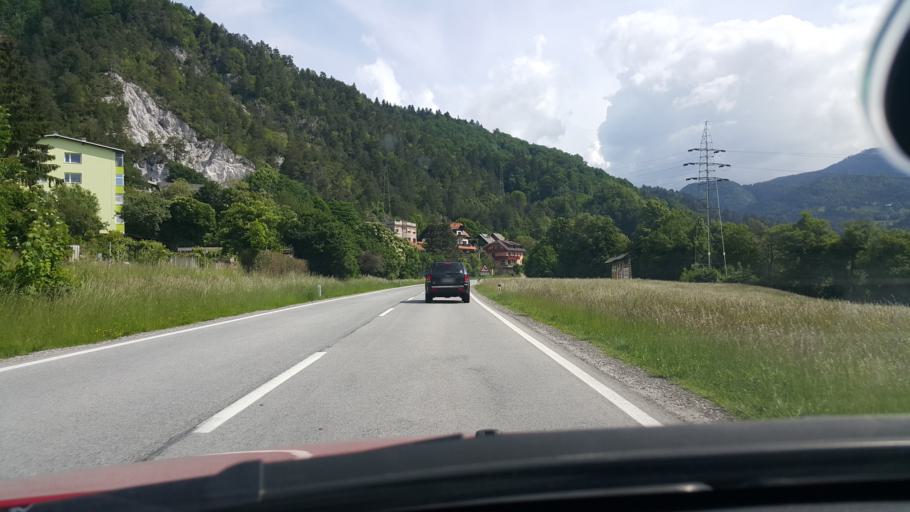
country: SI
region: Trzic
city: Bistrica pri Trzicu
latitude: 46.3571
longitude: 14.2948
